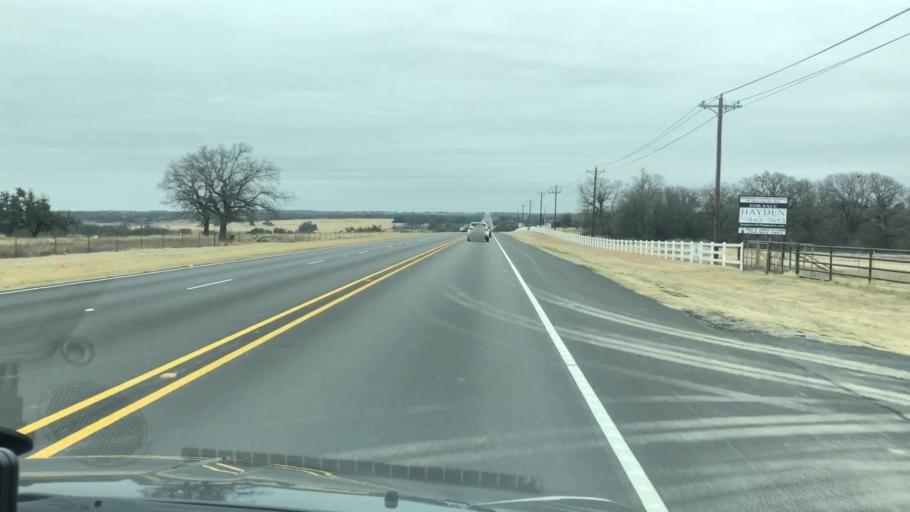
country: US
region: Texas
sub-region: Erath County
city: Stephenville
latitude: 32.2953
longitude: -98.1893
